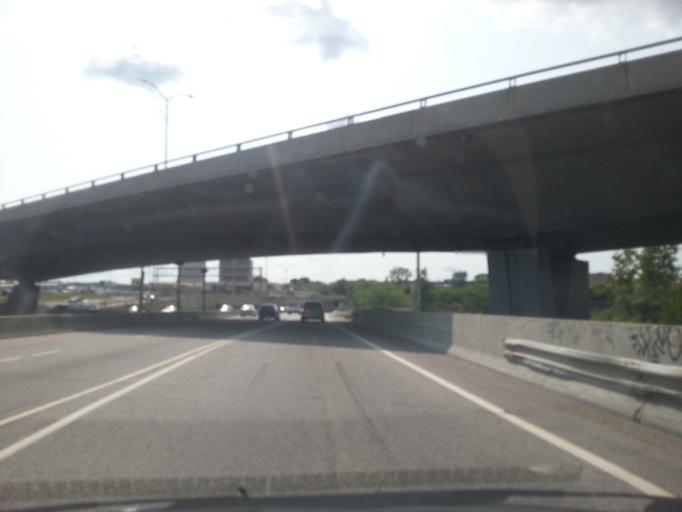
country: CA
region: Ontario
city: Ottawa
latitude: 45.4411
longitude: -75.7241
